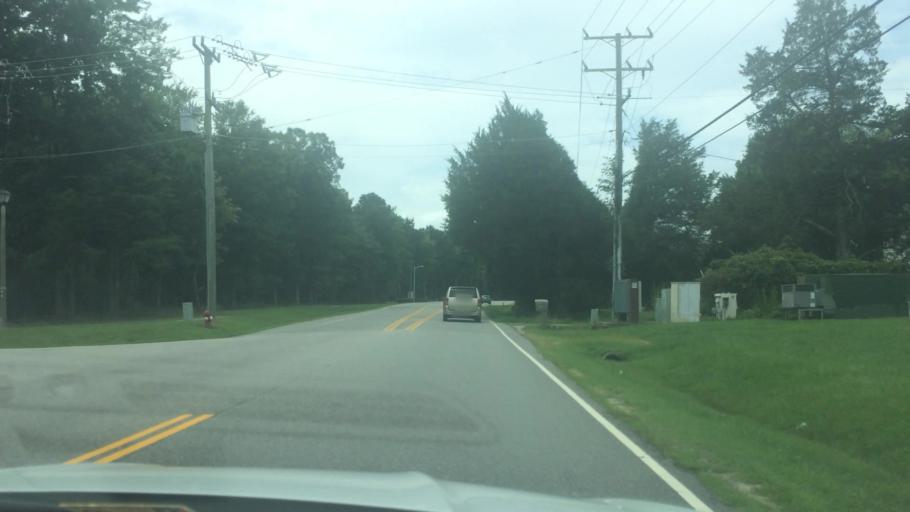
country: US
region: Virginia
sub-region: James City County
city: Williamsburg
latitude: 37.2662
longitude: -76.7596
